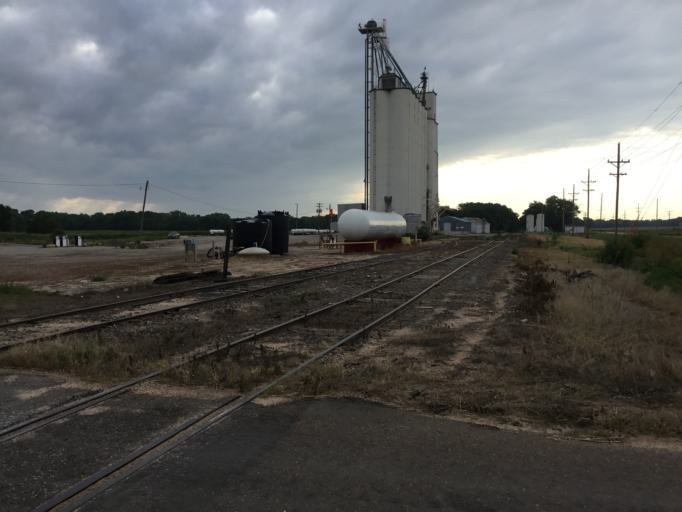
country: US
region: Kansas
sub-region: Pratt County
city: Pratt
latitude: 37.6520
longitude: -98.5568
